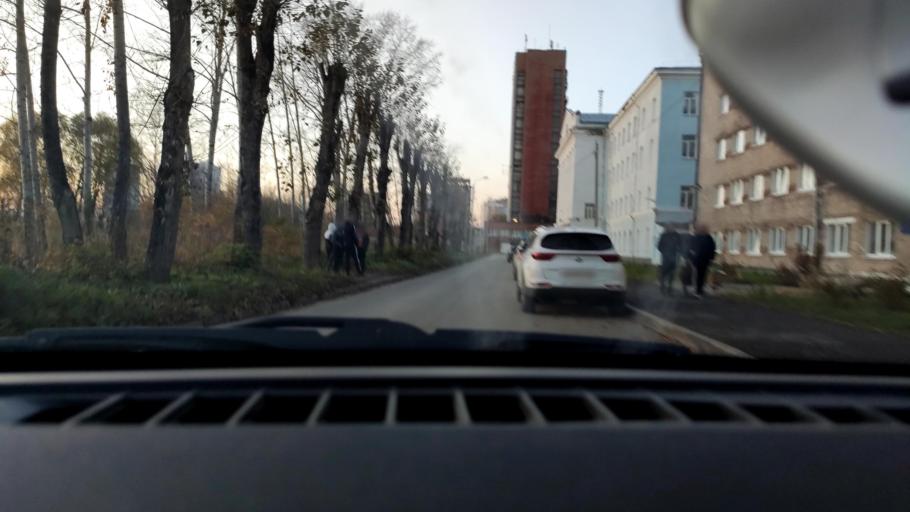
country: RU
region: Perm
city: Perm
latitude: 58.0167
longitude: 56.2749
